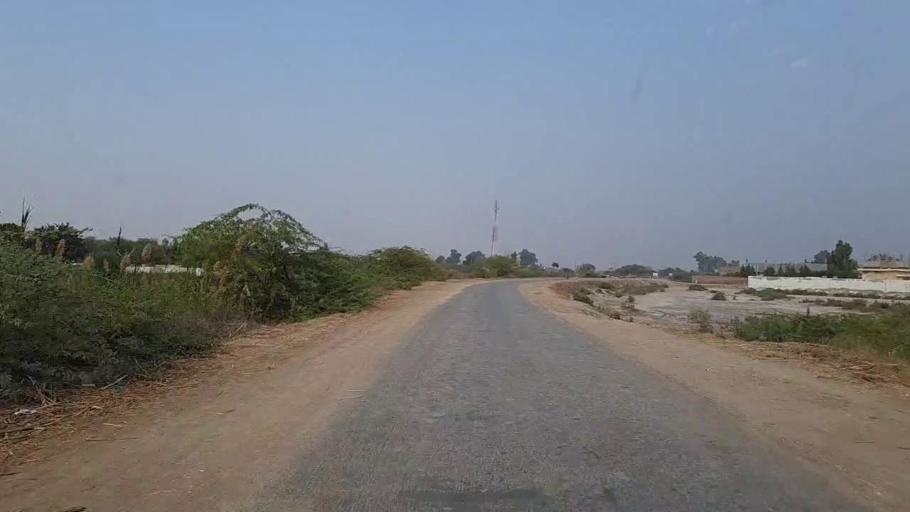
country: PK
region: Sindh
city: Mirwah Gorchani
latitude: 25.4243
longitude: 69.1512
